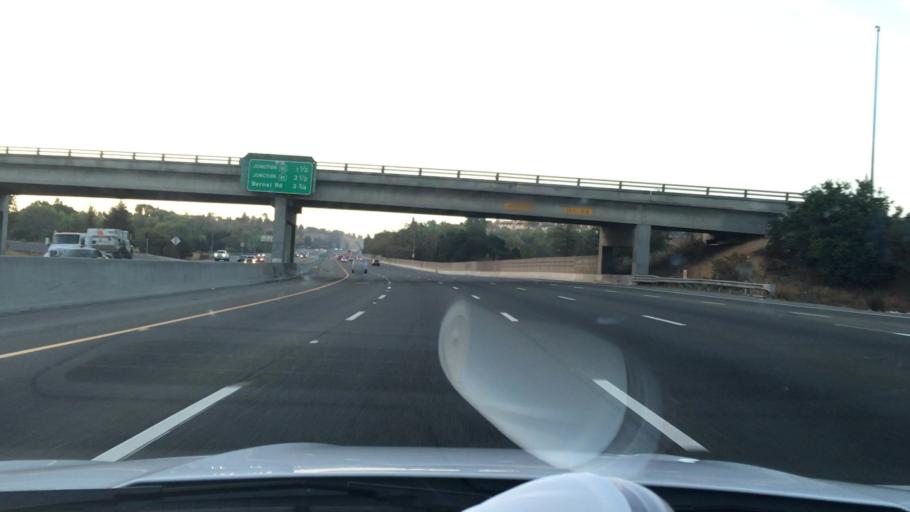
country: US
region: California
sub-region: Santa Clara County
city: Seven Trees
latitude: 37.2824
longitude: -121.8089
